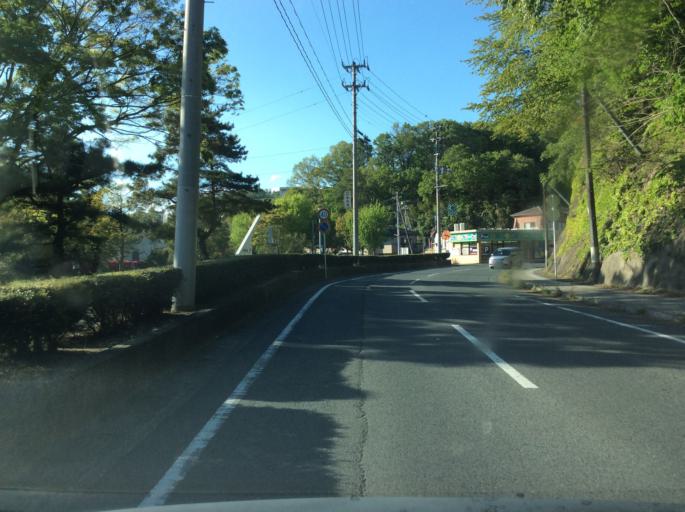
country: JP
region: Fukushima
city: Iwaki
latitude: 37.0042
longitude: 140.8404
